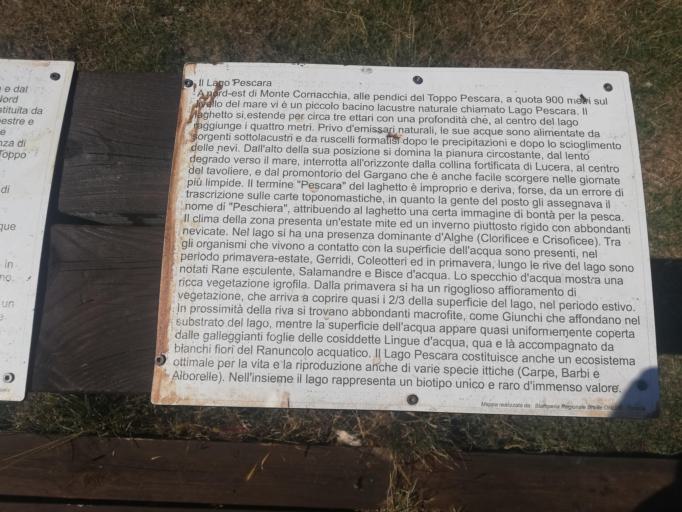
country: IT
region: Apulia
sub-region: Provincia di Foggia
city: Biccari
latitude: 41.3703
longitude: 15.1702
